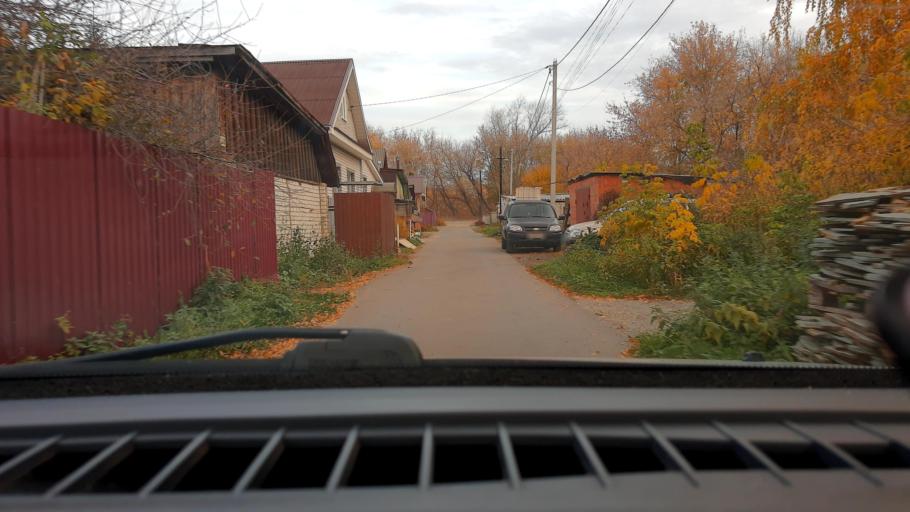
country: RU
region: Nizjnij Novgorod
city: Afonino
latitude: 56.2925
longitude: 44.1032
